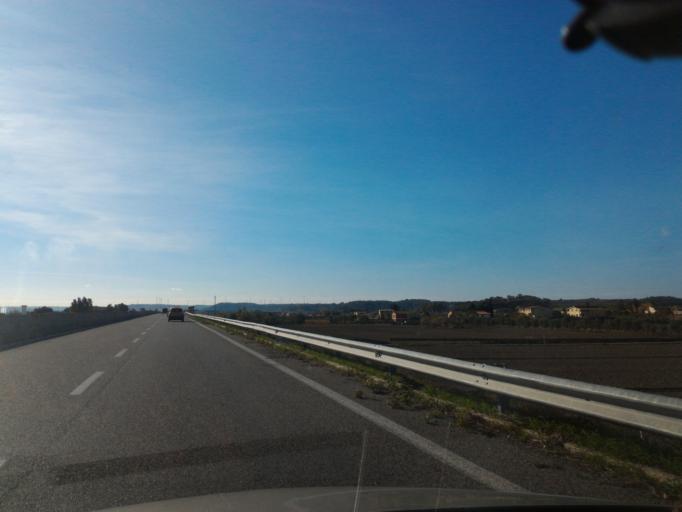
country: IT
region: Calabria
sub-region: Provincia di Crotone
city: Crotone
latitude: 39.1475
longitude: 17.0963
